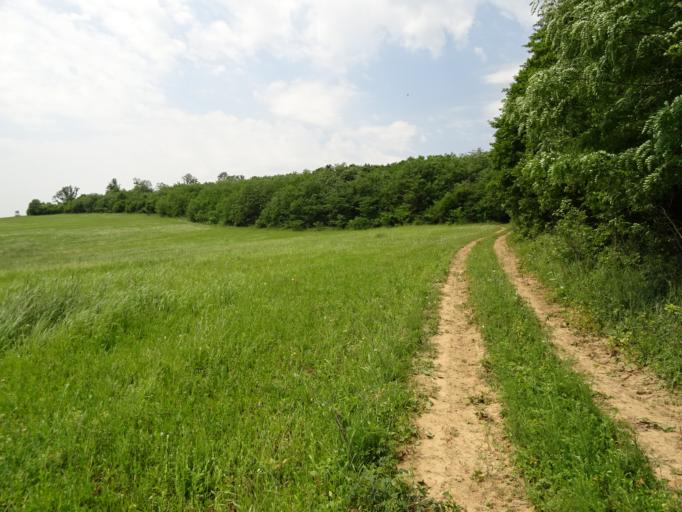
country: HU
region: Borsod-Abauj-Zemplen
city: Szendro
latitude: 48.5355
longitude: 20.8230
